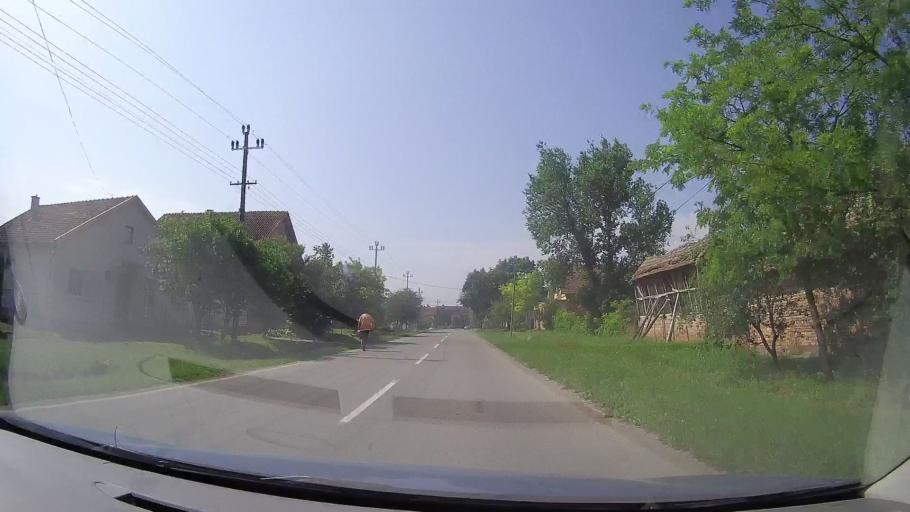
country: RS
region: Autonomna Pokrajina Vojvodina
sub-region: Srednjebanatski Okrug
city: Secanj
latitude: 45.3692
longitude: 20.7771
